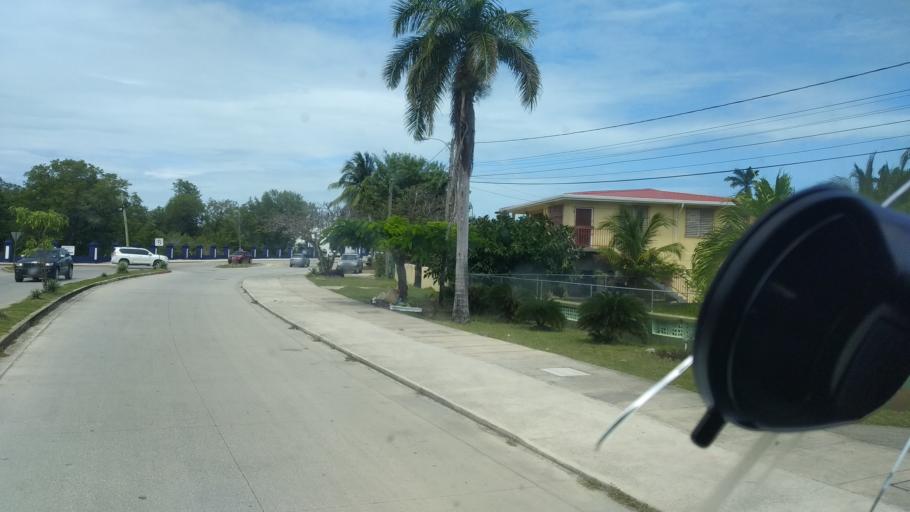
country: BZ
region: Belize
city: Belize City
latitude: 17.5099
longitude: -88.1989
